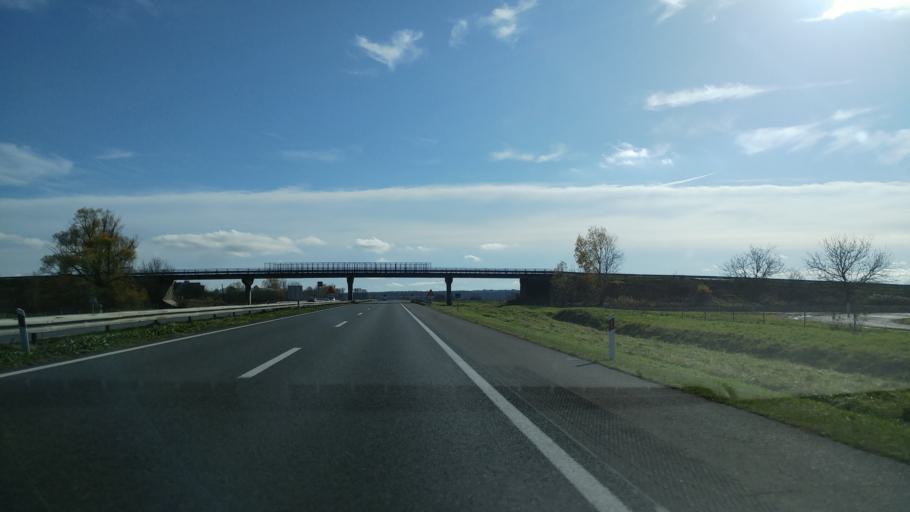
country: HR
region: Sisacko-Moslavacka
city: Lipovljani
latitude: 45.3898
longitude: 16.8673
